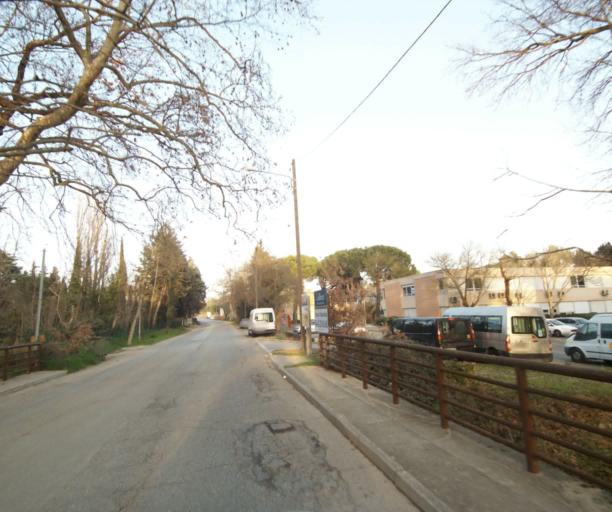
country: FR
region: Provence-Alpes-Cote d'Azur
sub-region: Departement des Bouches-du-Rhone
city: Vitrolles
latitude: 43.4316
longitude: 5.2752
